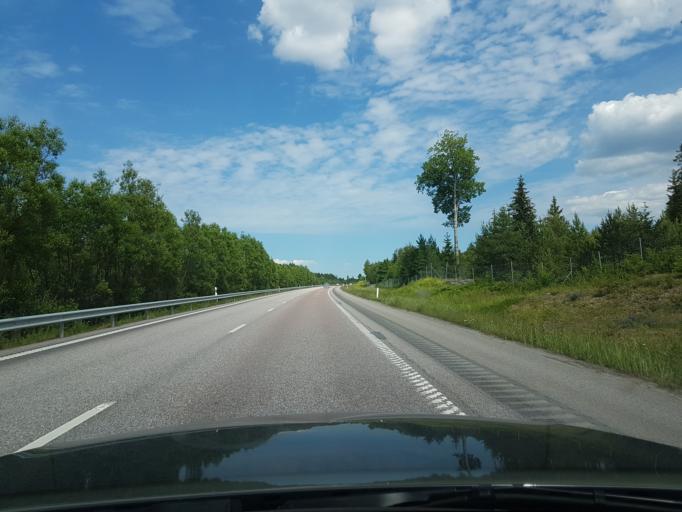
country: SE
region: Stockholm
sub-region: Norrtalje Kommun
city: Rimbo
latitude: 59.6594
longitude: 18.3678
